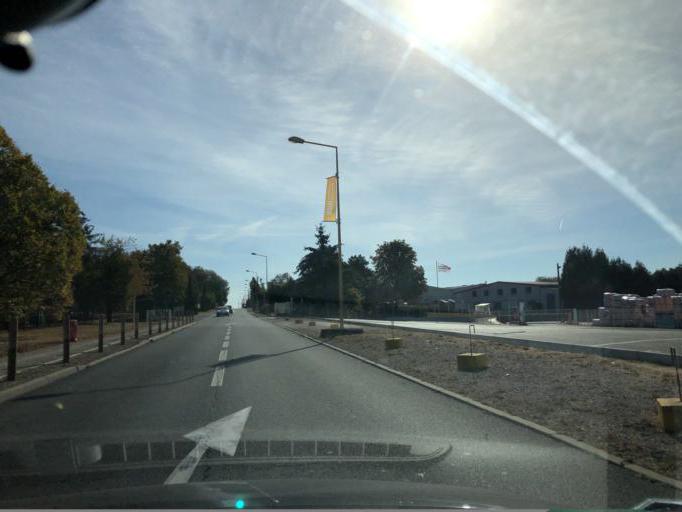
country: FR
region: Centre
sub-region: Departement du Loiret
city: Malesherbes
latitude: 48.2976
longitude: 2.3882
